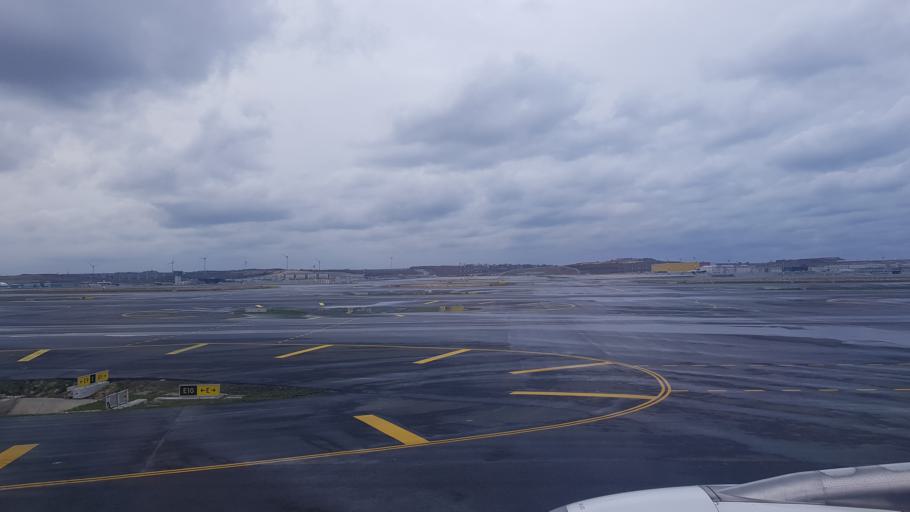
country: TR
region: Istanbul
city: Durusu
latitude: 41.2670
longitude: 28.7334
